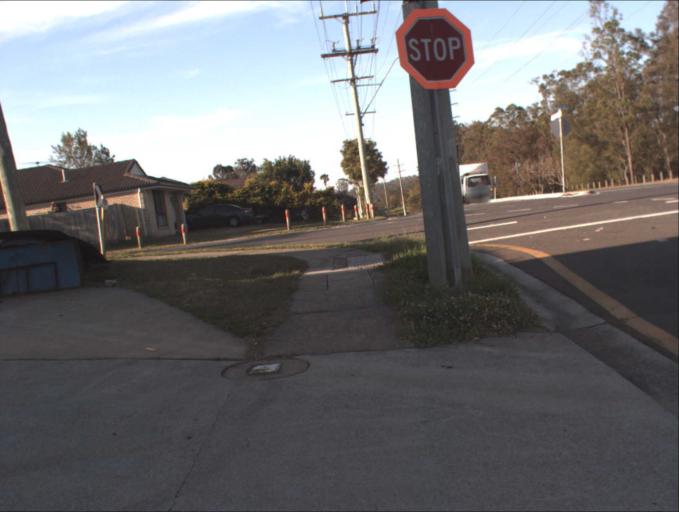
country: AU
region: Queensland
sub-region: Logan
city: Slacks Creek
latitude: -27.6527
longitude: 153.1350
